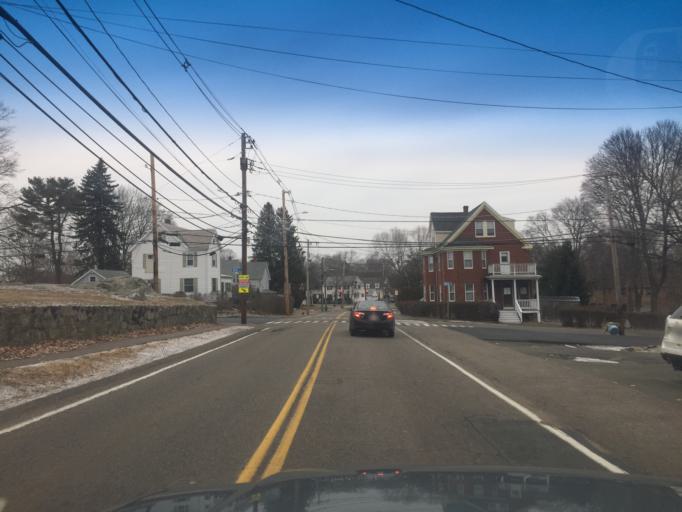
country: US
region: Massachusetts
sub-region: Norfolk County
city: Norwood
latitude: 42.1900
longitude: -71.1922
